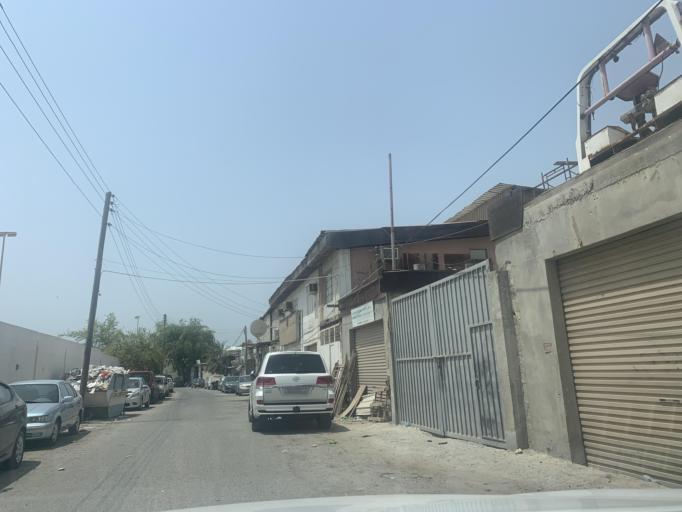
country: BH
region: Manama
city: Jidd Hafs
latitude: 26.2256
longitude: 50.4624
